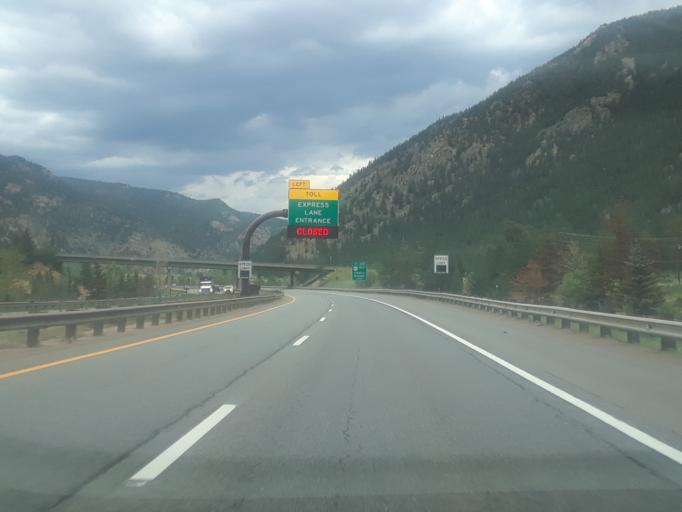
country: US
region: Colorado
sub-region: Clear Creek County
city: Georgetown
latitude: 39.7510
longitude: -105.6638
